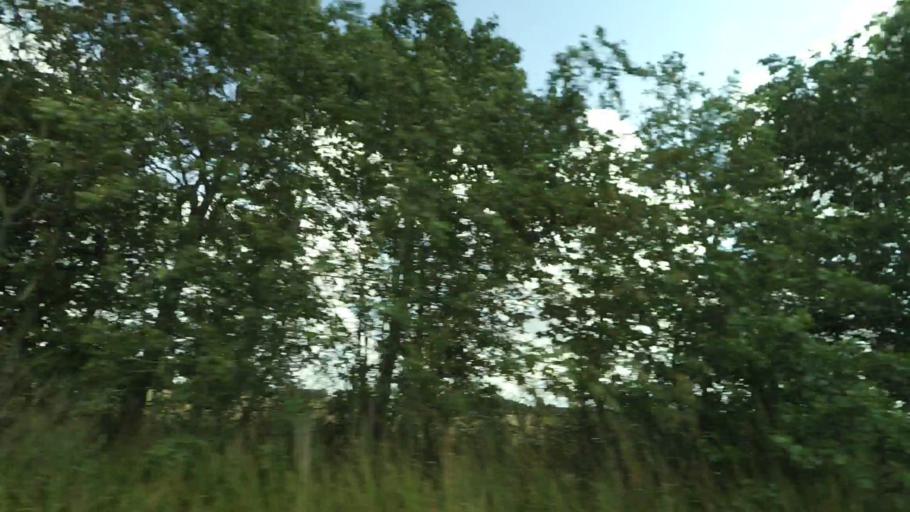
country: DK
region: Central Jutland
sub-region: Norddjurs Kommune
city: Auning
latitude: 56.5029
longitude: 10.4267
